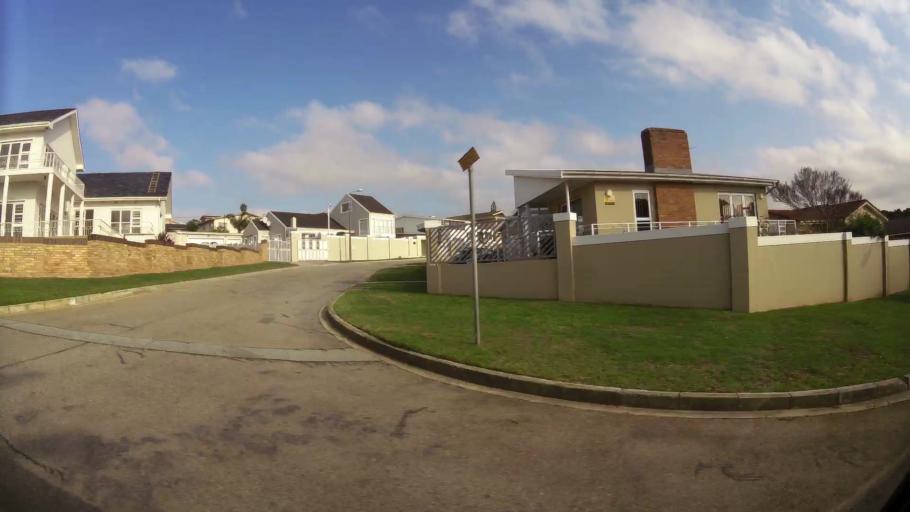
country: ZA
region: Eastern Cape
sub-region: Nelson Mandela Bay Metropolitan Municipality
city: Port Elizabeth
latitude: -33.9260
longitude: 25.5549
